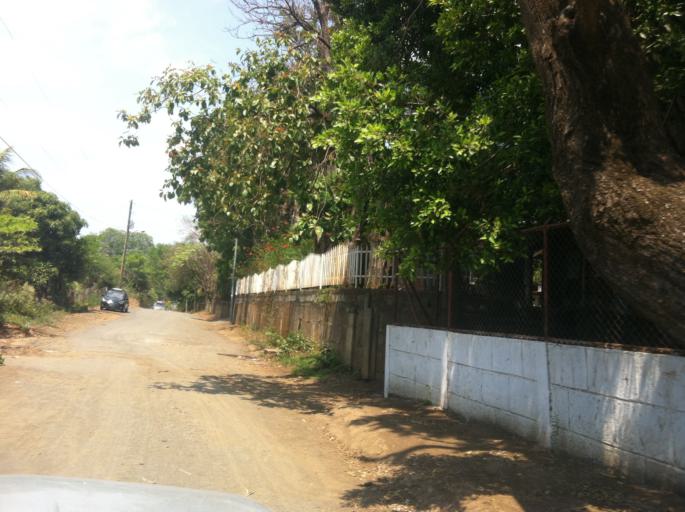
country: NI
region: Managua
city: Ciudad Sandino
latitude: 12.1036
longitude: -86.3318
